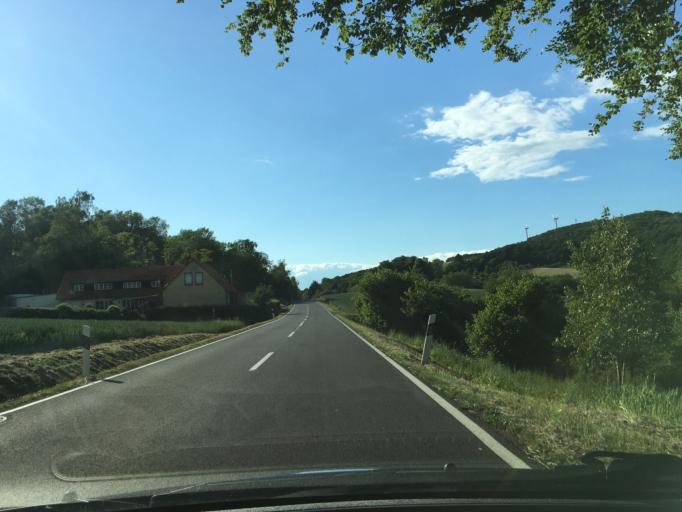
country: DE
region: Lower Saxony
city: Coppengrave
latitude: 51.9768
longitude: 9.7520
